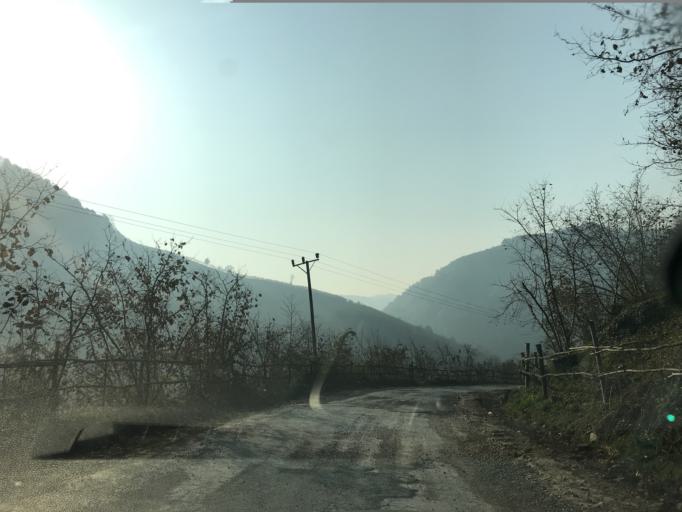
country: TR
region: Duzce
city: Cumayeri
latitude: 40.9366
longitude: 30.9292
